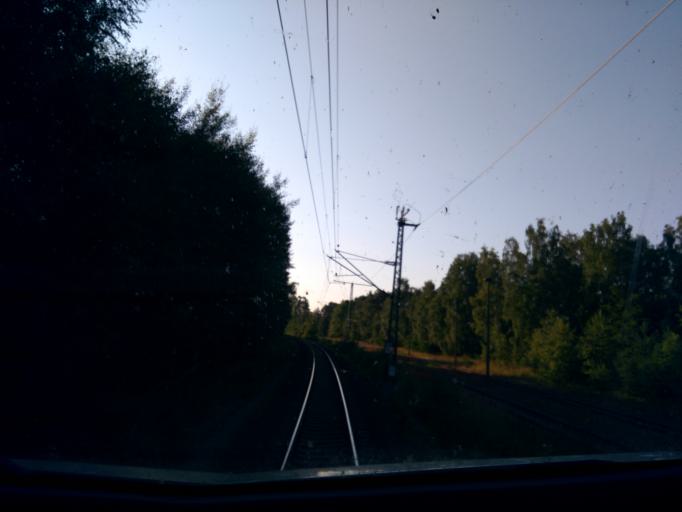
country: DE
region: Brandenburg
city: Vetschau
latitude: 51.7845
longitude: 14.0974
